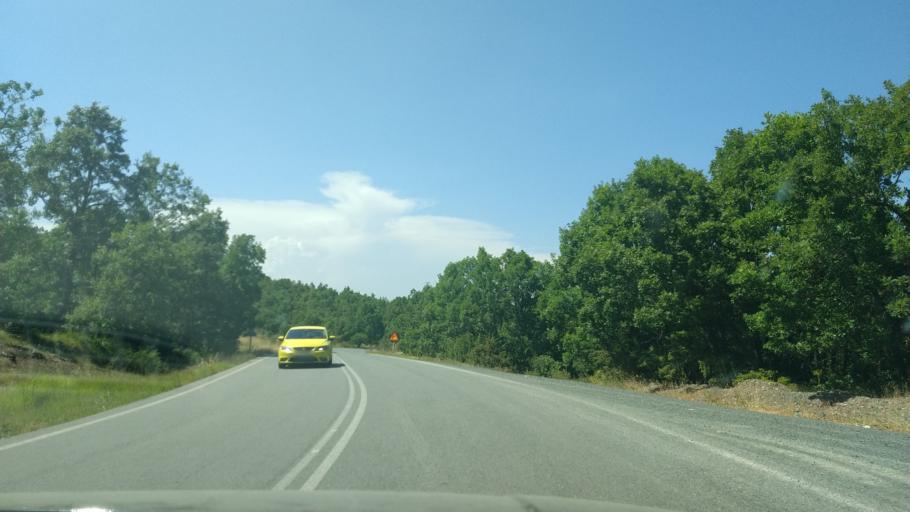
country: GR
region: West Macedonia
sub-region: Nomos Grevenon
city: Grevena
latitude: 40.0176
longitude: 21.4875
